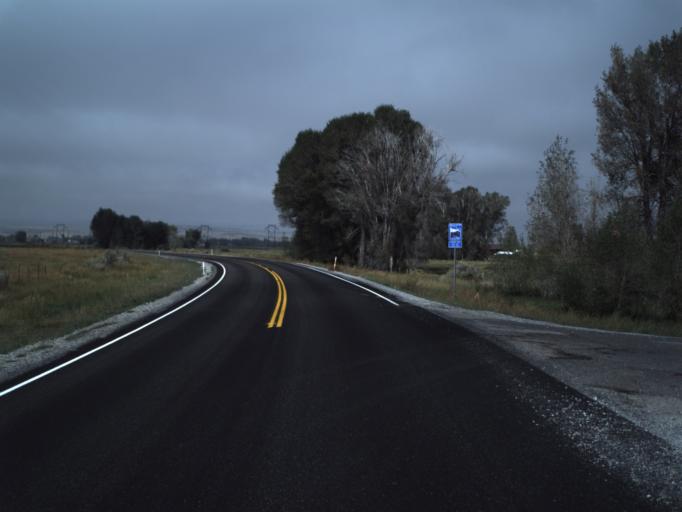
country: US
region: Utah
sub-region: Rich County
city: Randolph
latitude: 41.5170
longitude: -111.1399
